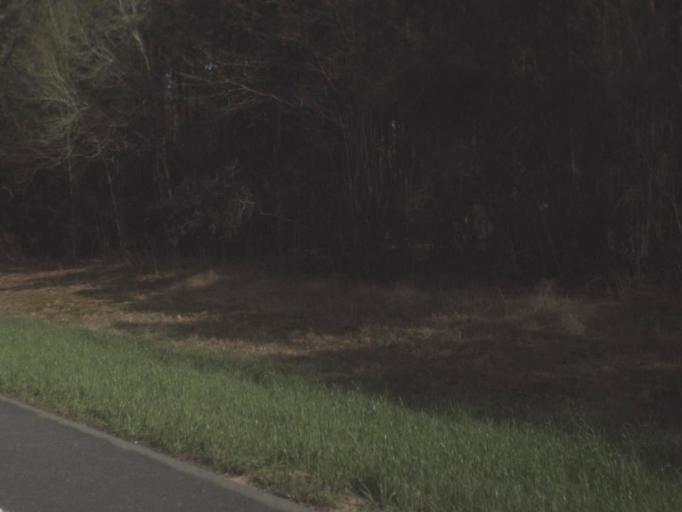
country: US
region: Florida
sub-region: Holmes County
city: Bonifay
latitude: 30.7942
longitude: -85.7294
